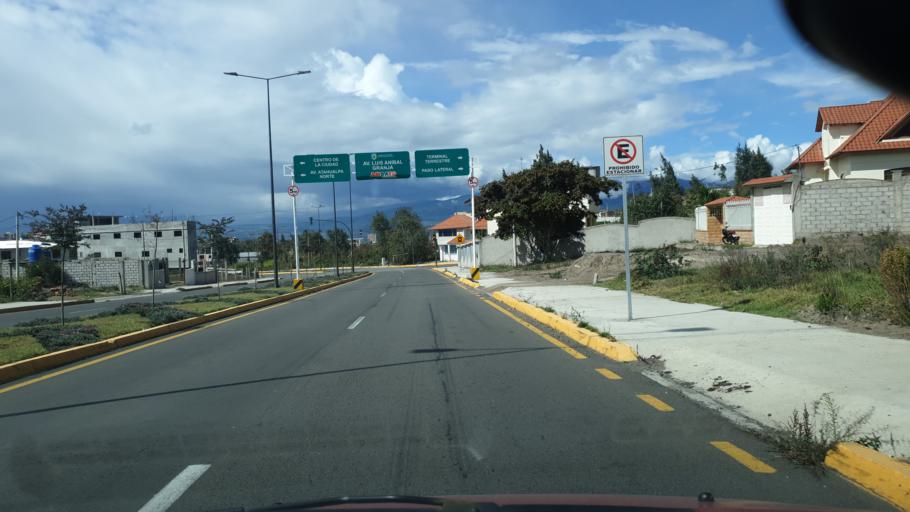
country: EC
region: Tungurahua
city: Ambato
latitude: -1.2910
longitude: -78.6308
